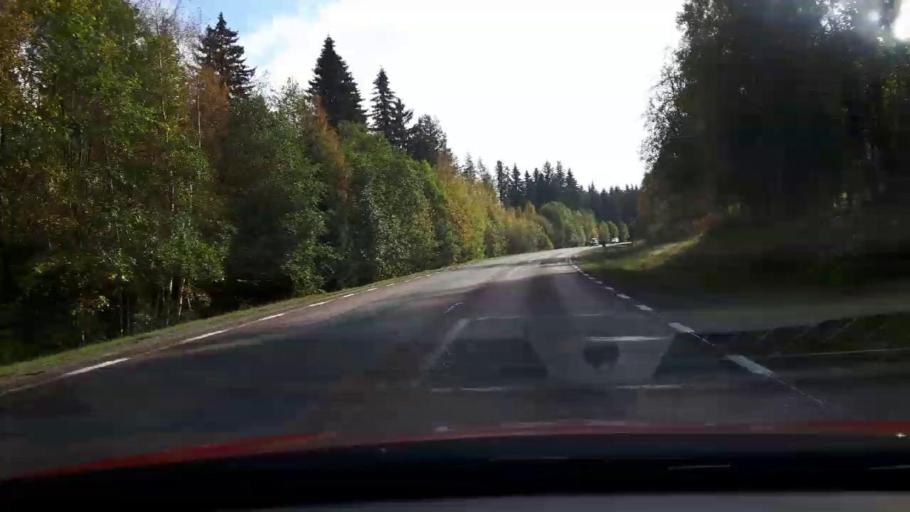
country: SE
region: Gaevleborg
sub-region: Ljusdals Kommun
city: Farila
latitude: 61.8856
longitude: 15.7022
